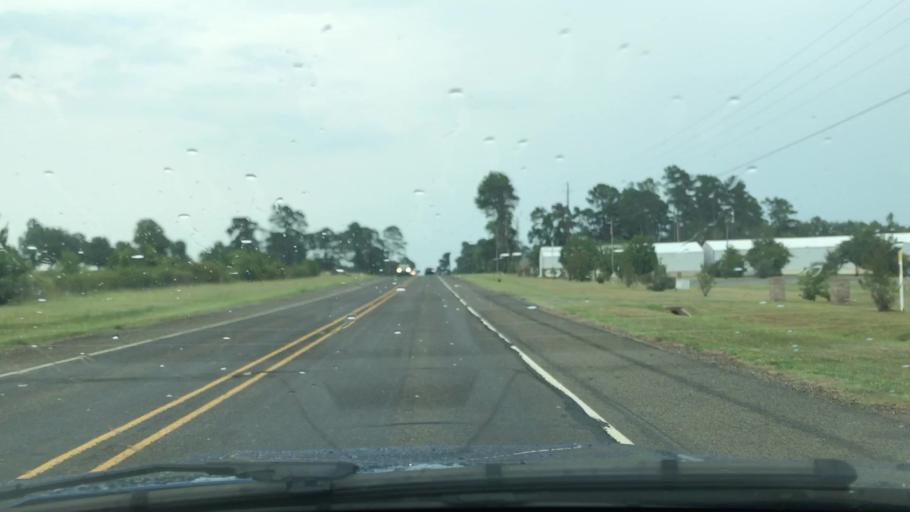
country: US
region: Texas
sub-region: Harrison County
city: Waskom
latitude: 32.4789
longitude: -94.0806
